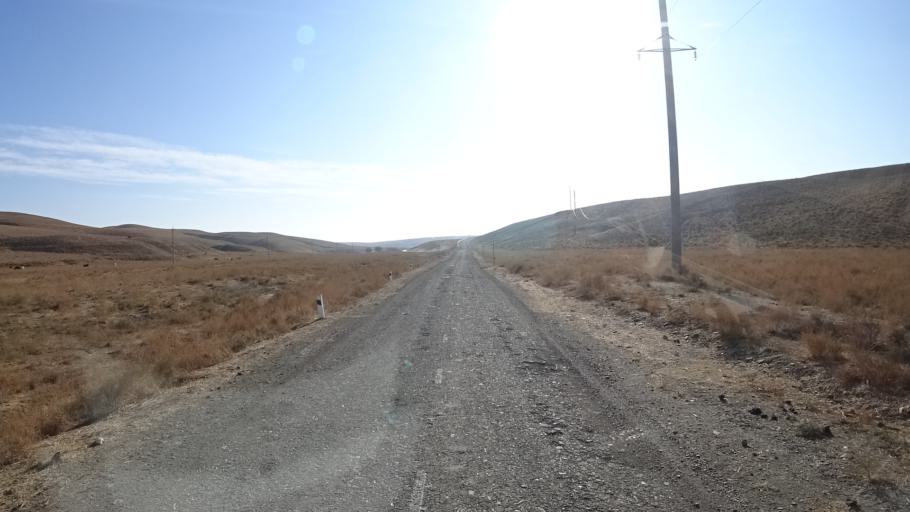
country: UZ
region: Navoiy
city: Karmana Shahri
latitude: 40.2770
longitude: 65.5809
